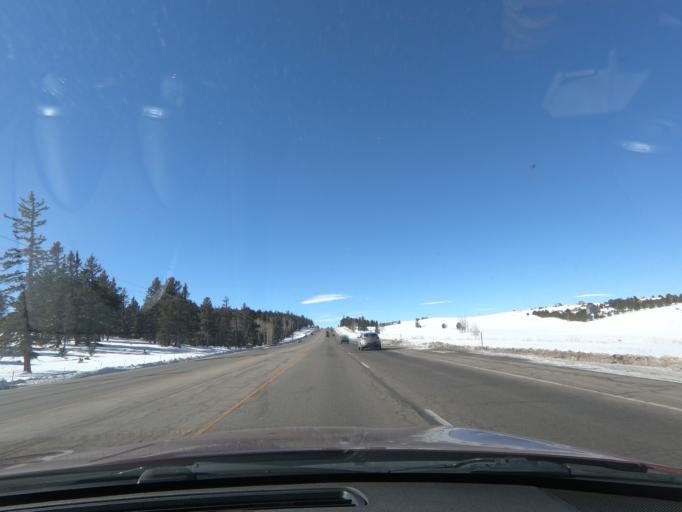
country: US
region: Colorado
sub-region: Teller County
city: Woodland Park
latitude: 38.9561
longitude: -105.1165
